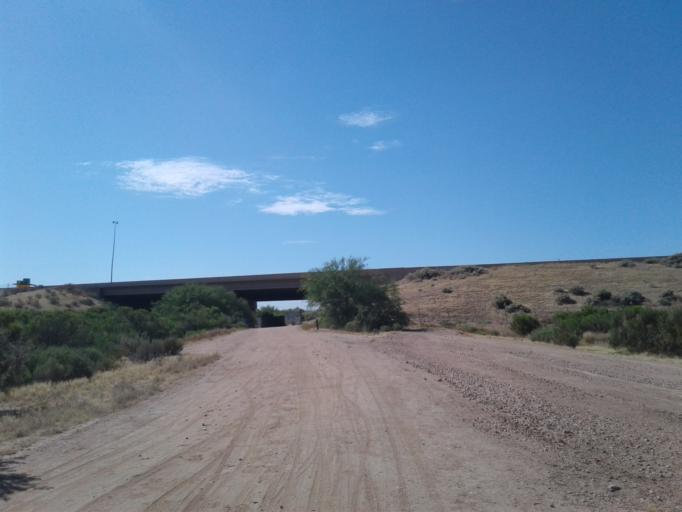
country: US
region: Arizona
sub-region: Maricopa County
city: Paradise Valley
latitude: 33.6739
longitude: -112.0092
